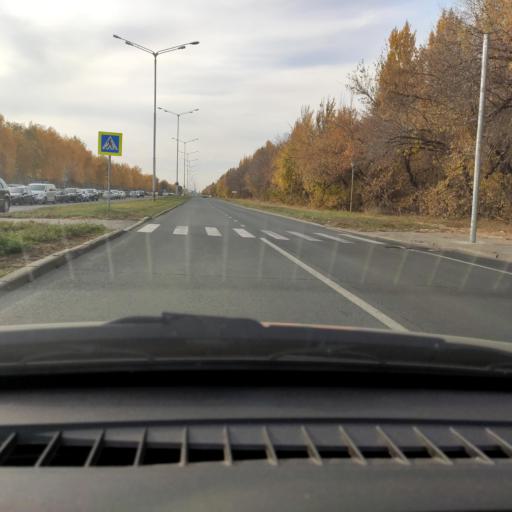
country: RU
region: Samara
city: Tol'yatti
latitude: 53.5707
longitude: 49.2448
